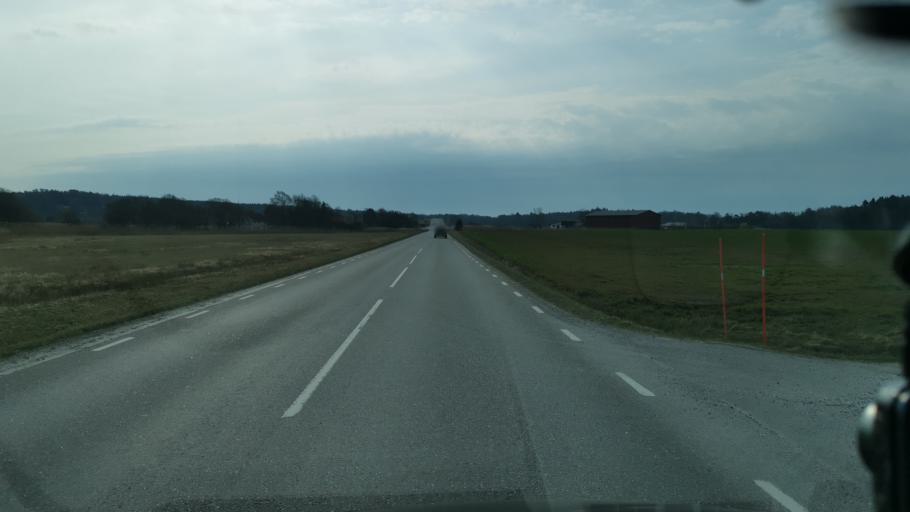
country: SE
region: Vaestra Goetaland
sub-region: Stenungsunds Kommun
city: Stora Hoga
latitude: 57.9797
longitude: 11.8261
